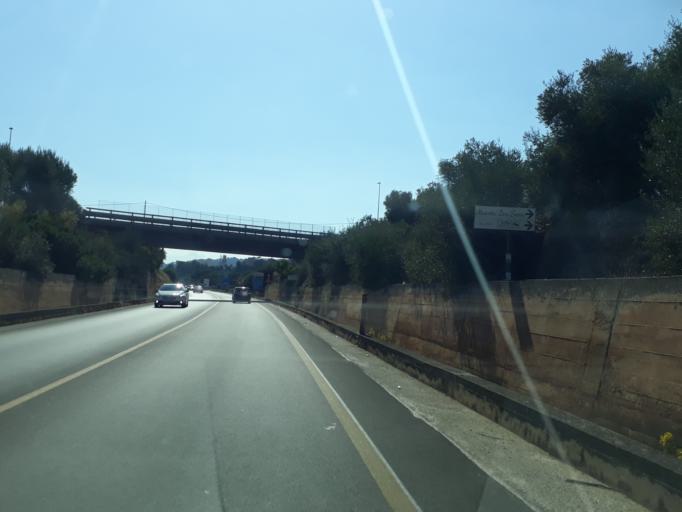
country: IT
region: Apulia
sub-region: Provincia di Brindisi
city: Fasano
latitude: 40.8351
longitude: 17.3501
